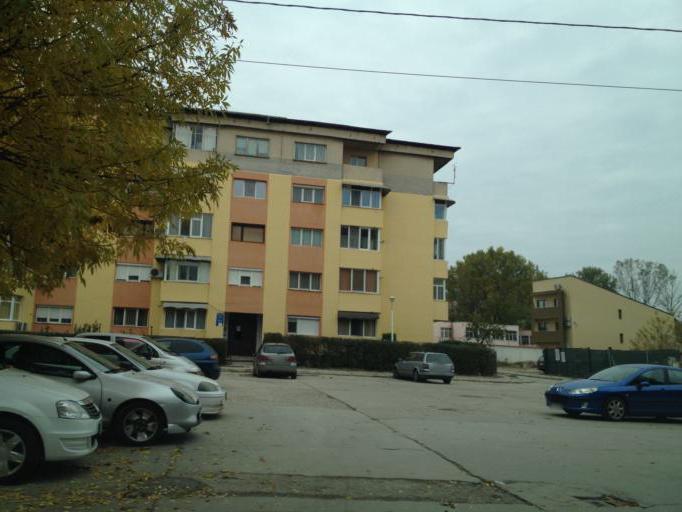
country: RO
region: Dolj
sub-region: Municipiul Craiova
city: Popoveni
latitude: 44.2991
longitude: 23.7923
